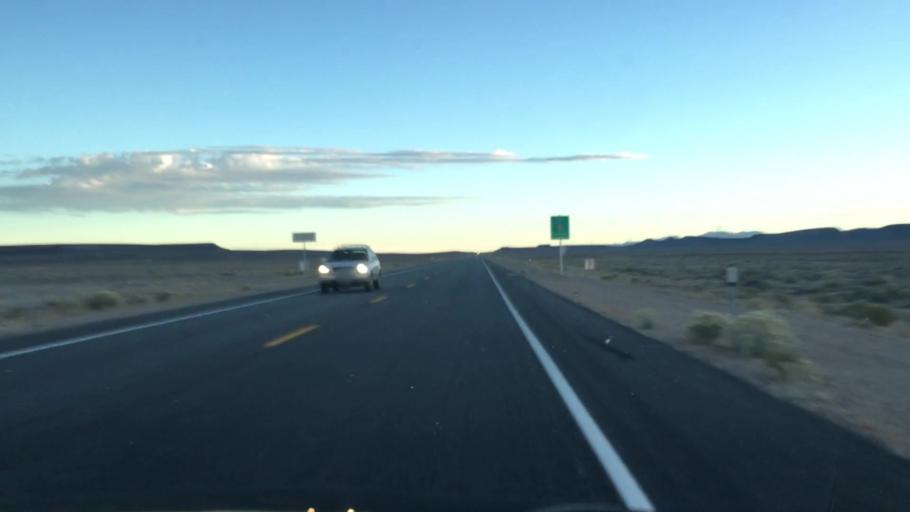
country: US
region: Nevada
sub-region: Esmeralda County
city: Goldfield
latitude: 37.4437
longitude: -117.1659
